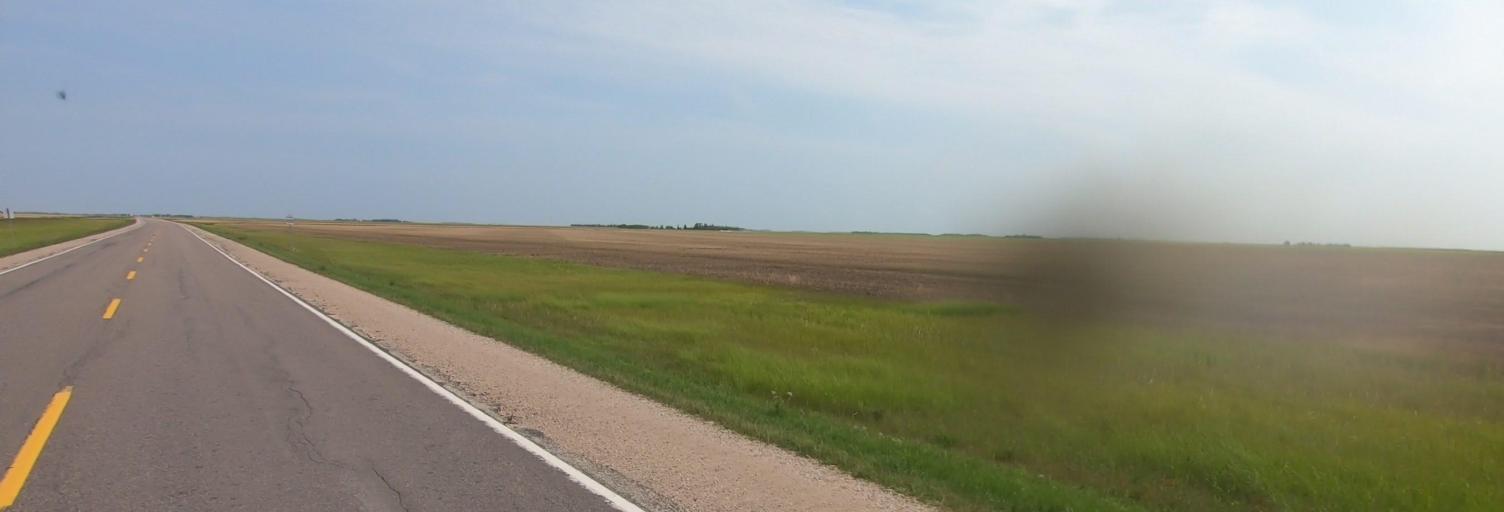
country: CA
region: Manitoba
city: Morris
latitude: 49.6162
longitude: -97.3198
